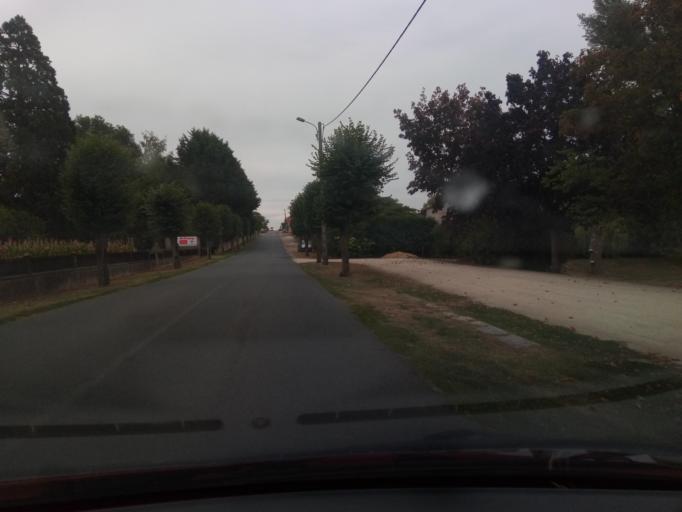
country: FR
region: Poitou-Charentes
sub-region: Departement de la Vienne
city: Saint-Savin
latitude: 46.5066
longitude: 0.7752
